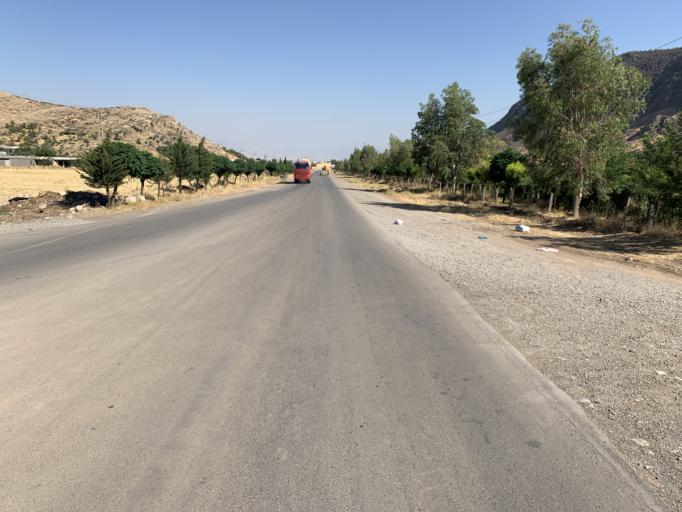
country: IQ
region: As Sulaymaniyah
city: Raniye
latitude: 36.2713
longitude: 44.8359
